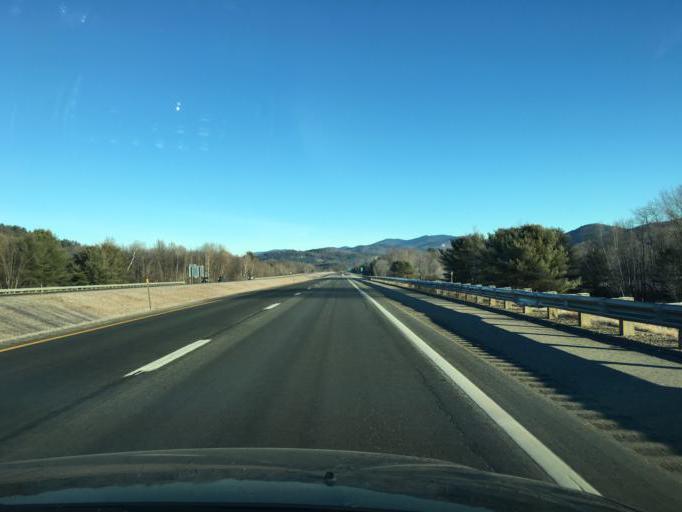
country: US
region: New Hampshire
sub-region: Grafton County
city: Thornton
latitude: 43.8247
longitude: -71.6579
